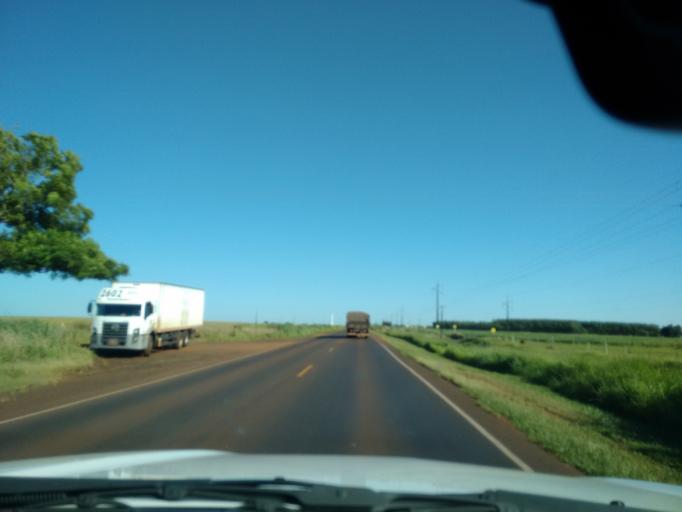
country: BR
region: Mato Grosso do Sul
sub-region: Dourados
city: Dourados
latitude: -22.3721
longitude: -54.7959
